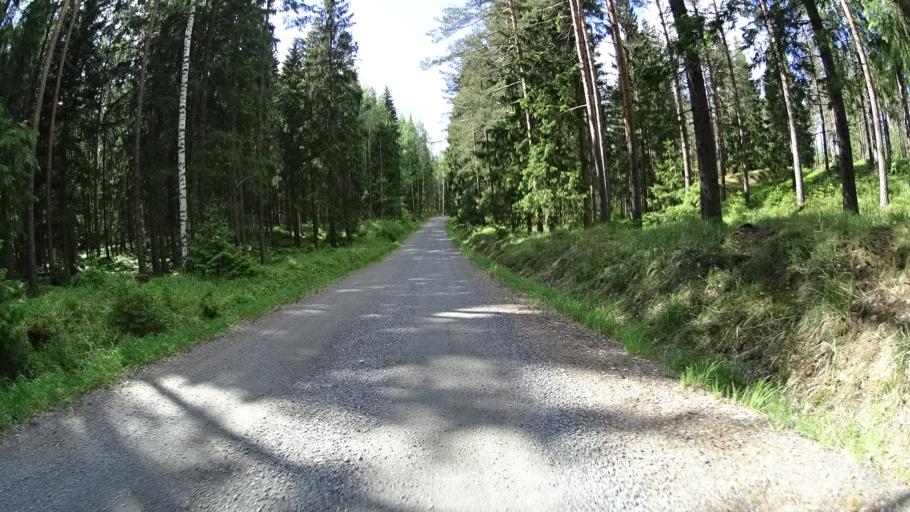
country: FI
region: Varsinais-Suomi
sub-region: Salo
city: Kisko
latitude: 60.1919
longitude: 23.5552
